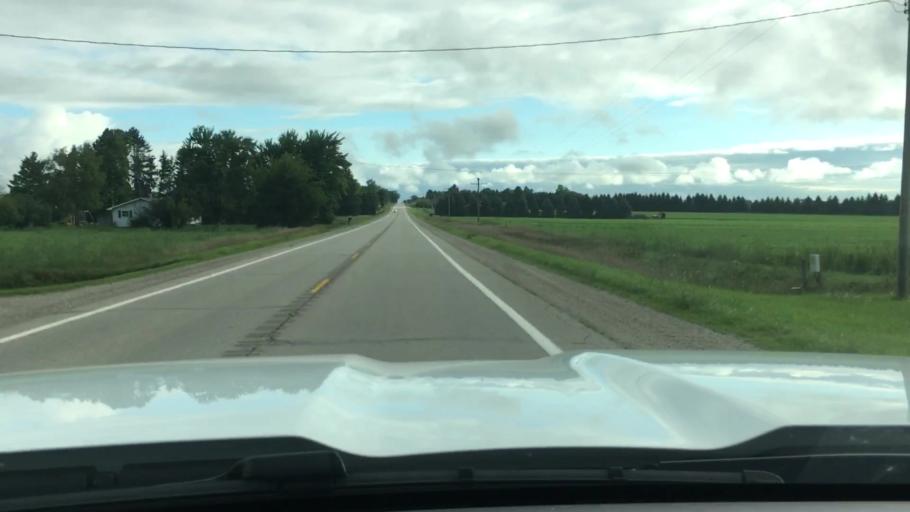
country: US
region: Michigan
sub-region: Tuscola County
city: Caro
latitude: 43.5414
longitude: -83.3372
